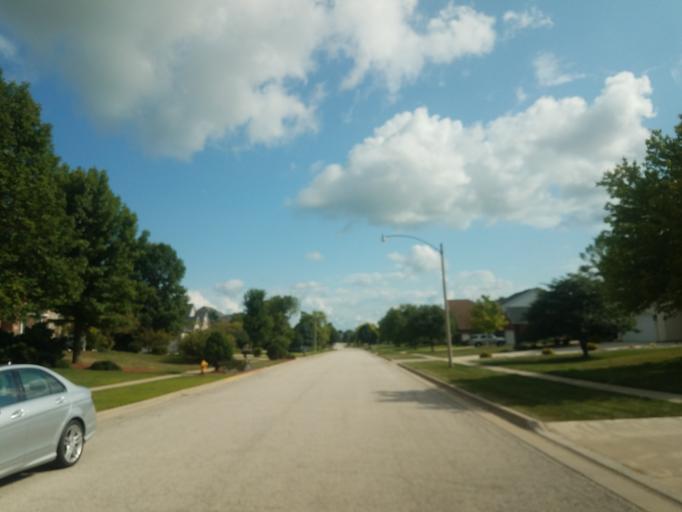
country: US
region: Illinois
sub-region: McLean County
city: Normal
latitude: 40.5072
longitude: -88.9132
